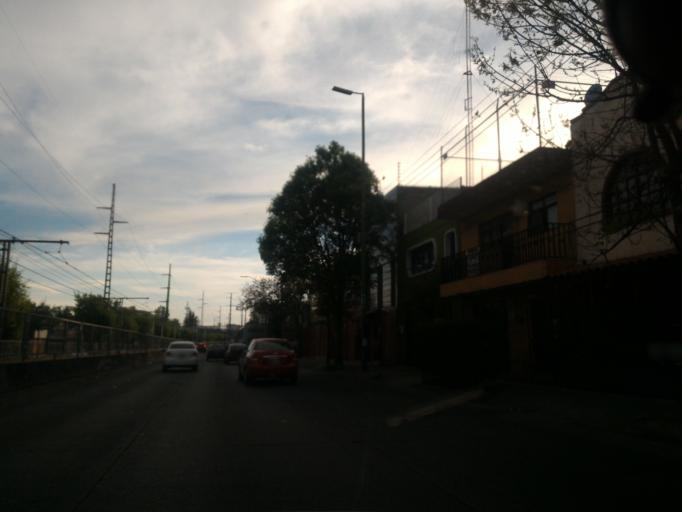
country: MX
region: Jalisco
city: Guadalajara
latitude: 20.6373
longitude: -103.3777
